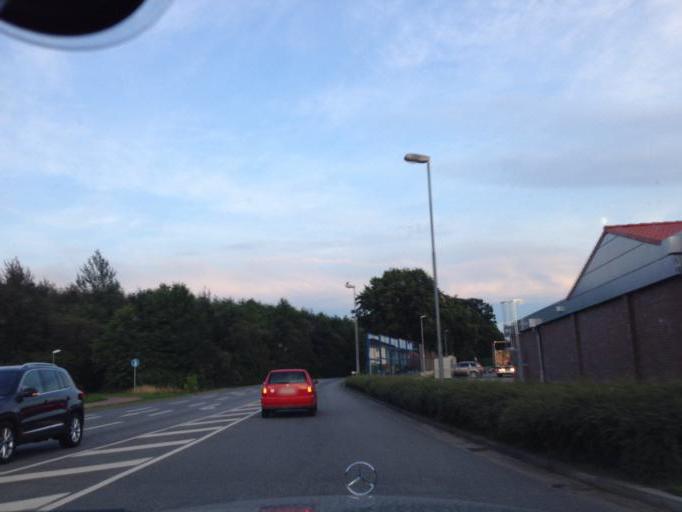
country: DE
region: Schleswig-Holstein
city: Bargteheide
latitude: 53.7235
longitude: 10.2542
